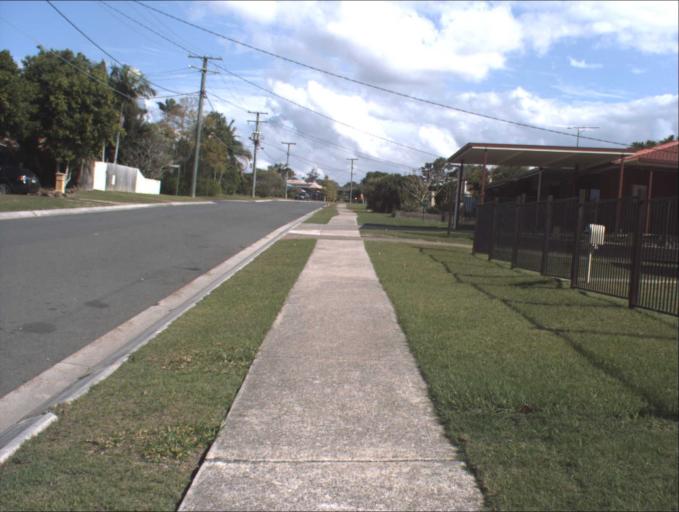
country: AU
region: Queensland
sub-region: Logan
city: Park Ridge South
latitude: -27.6924
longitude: 153.0161
